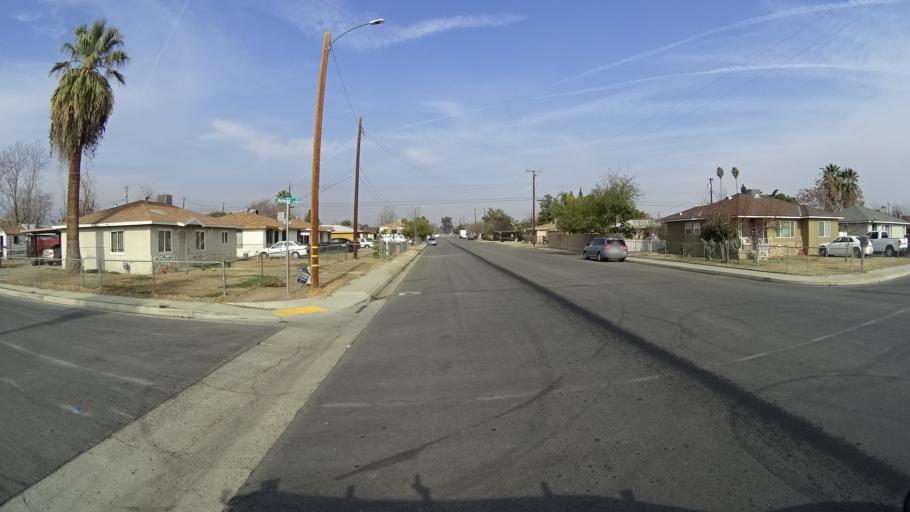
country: US
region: California
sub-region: Kern County
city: Bakersfield
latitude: 35.3701
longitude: -118.9887
